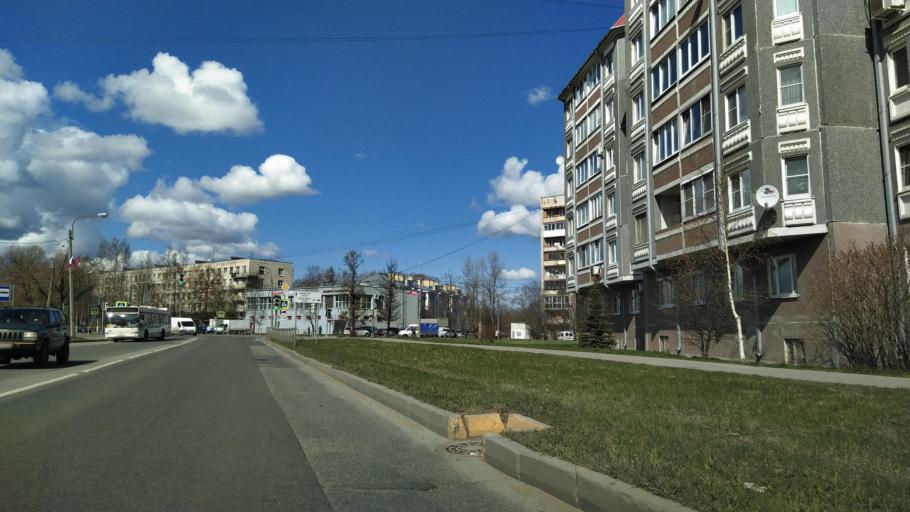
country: RU
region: St.-Petersburg
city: Pushkin
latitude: 59.7032
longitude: 30.3734
